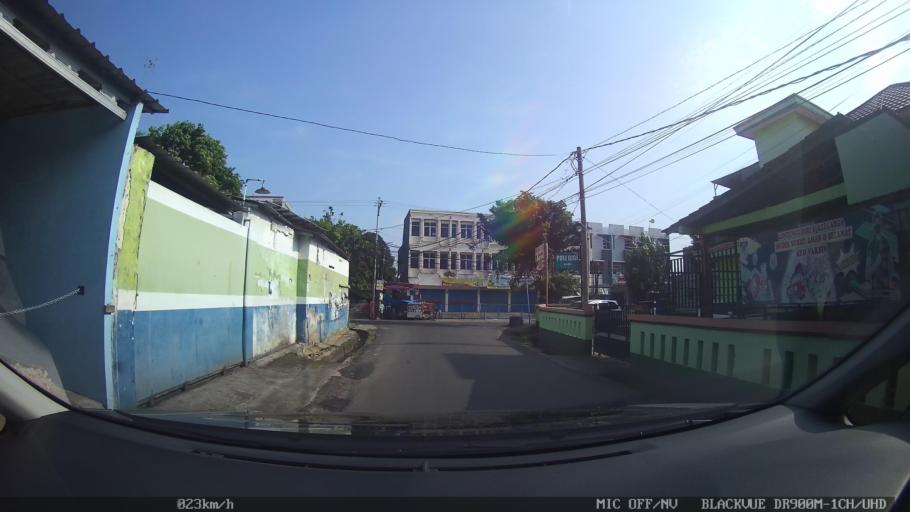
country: ID
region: Lampung
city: Kedaton
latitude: -5.3873
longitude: 105.2638
